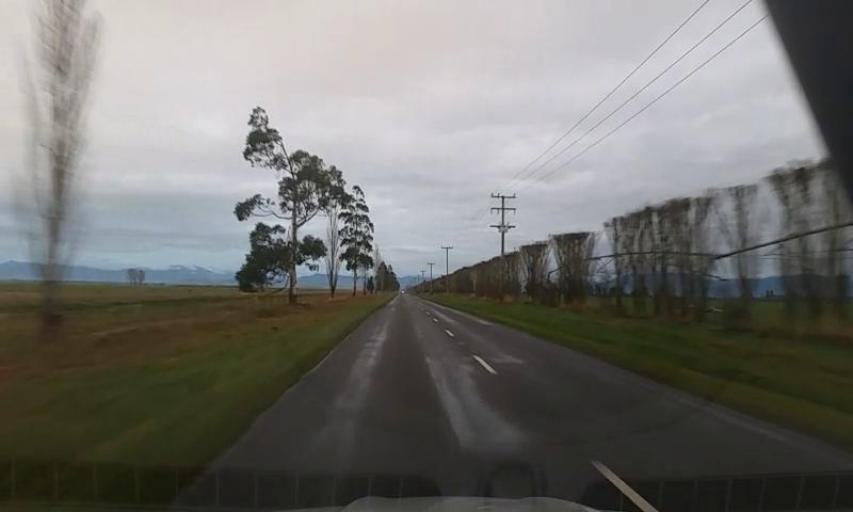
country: NZ
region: Canterbury
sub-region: Ashburton District
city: Methven
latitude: -43.7400
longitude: 171.6883
